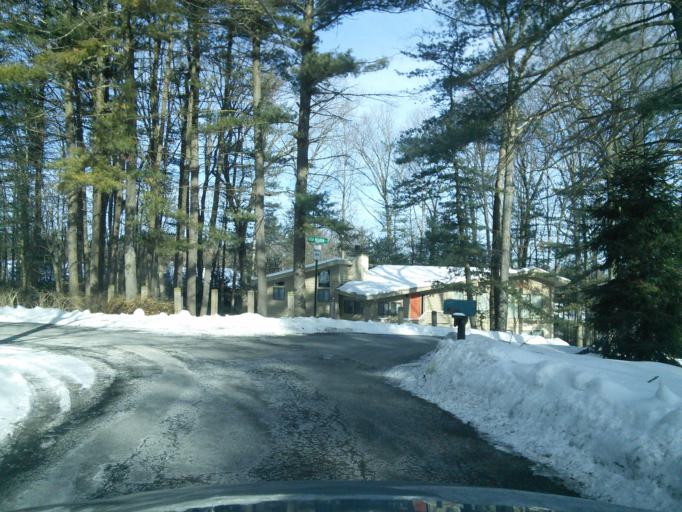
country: US
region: Pennsylvania
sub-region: Centre County
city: Park Forest Village
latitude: 40.8296
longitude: -77.8822
